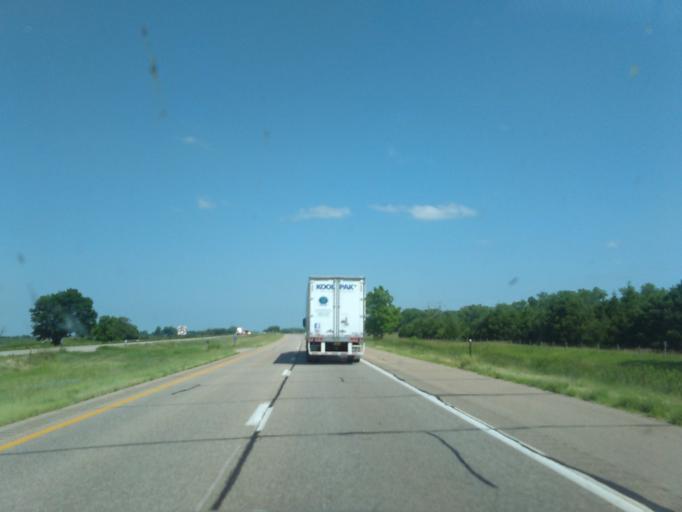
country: US
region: Nebraska
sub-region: Buffalo County
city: Kearney
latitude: 40.6850
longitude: -99.3182
